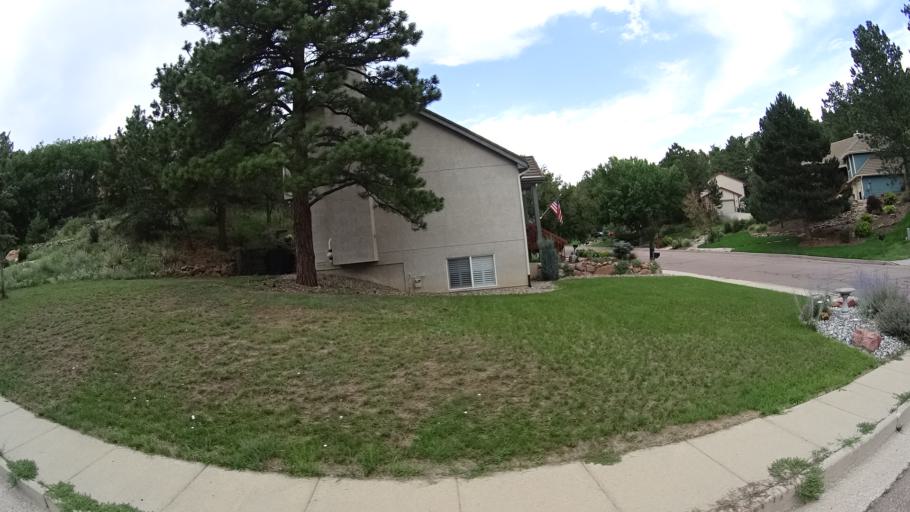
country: US
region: Colorado
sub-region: El Paso County
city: Colorado Springs
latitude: 38.9083
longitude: -104.8392
